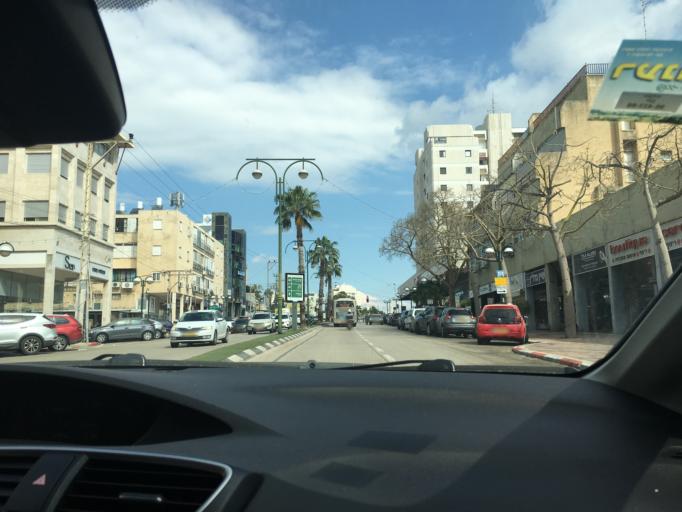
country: IL
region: Tel Aviv
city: Ramat HaSharon
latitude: 32.1476
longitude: 34.8392
